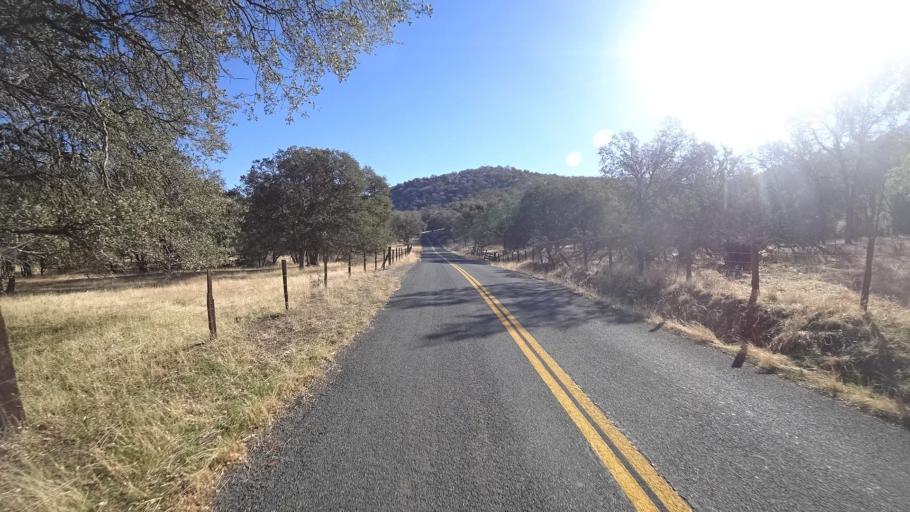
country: US
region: California
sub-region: Kern County
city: Alta Sierra
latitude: 35.7864
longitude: -118.7599
